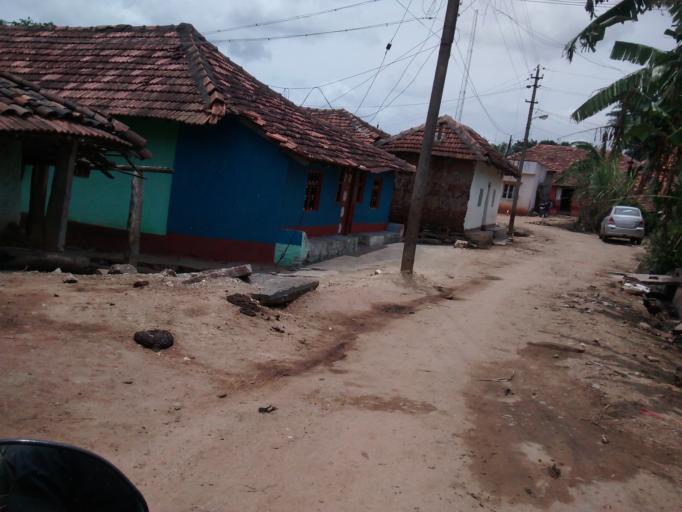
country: IN
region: Karnataka
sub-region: Hassan
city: Hassan
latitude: 12.9069
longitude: 76.1283
